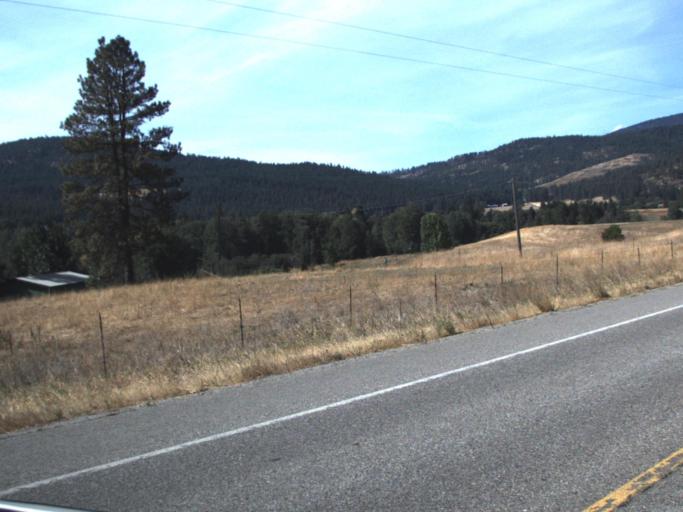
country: US
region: Washington
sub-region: Stevens County
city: Chewelah
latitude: 48.3145
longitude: -117.8065
